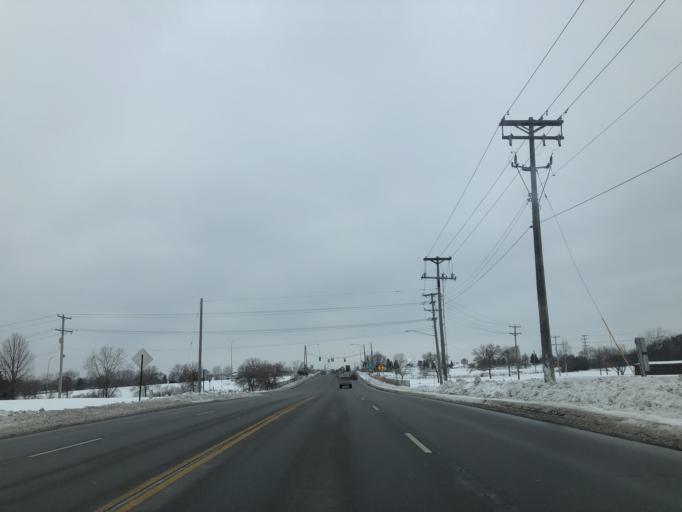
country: US
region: Minnesota
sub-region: Hennepin County
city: Osseo
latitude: 45.0946
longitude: -93.3984
